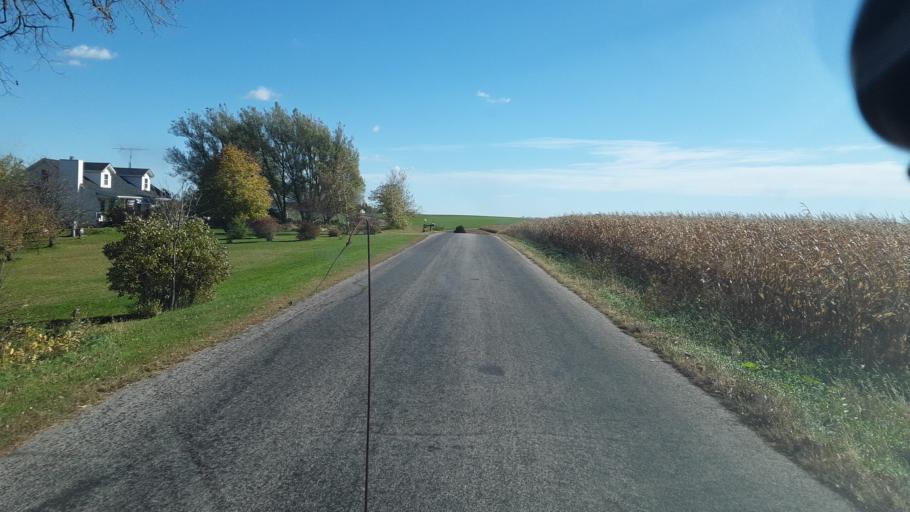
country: US
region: Wisconsin
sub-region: Vernon County
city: Hillsboro
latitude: 43.6891
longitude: -90.4273
